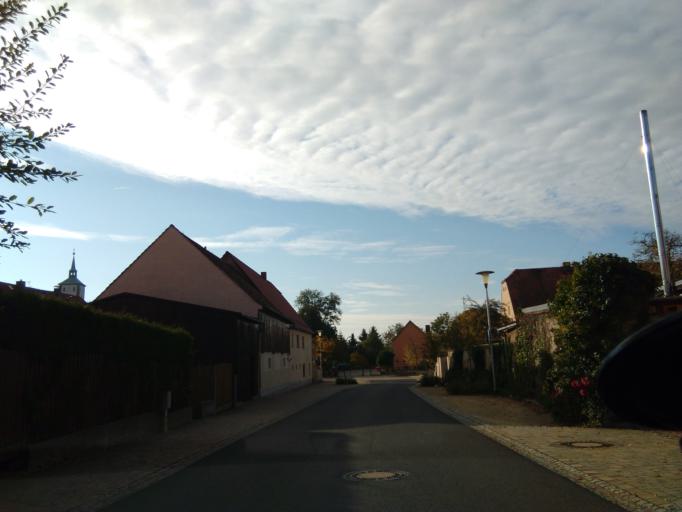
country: DE
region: Saxony
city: Meissen
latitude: 51.1987
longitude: 13.4266
